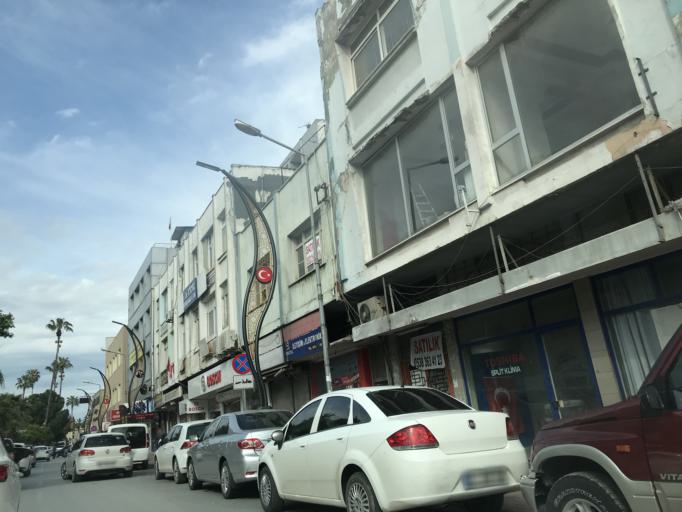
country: TR
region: Mersin
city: Tarsus
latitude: 36.9154
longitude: 34.8940
